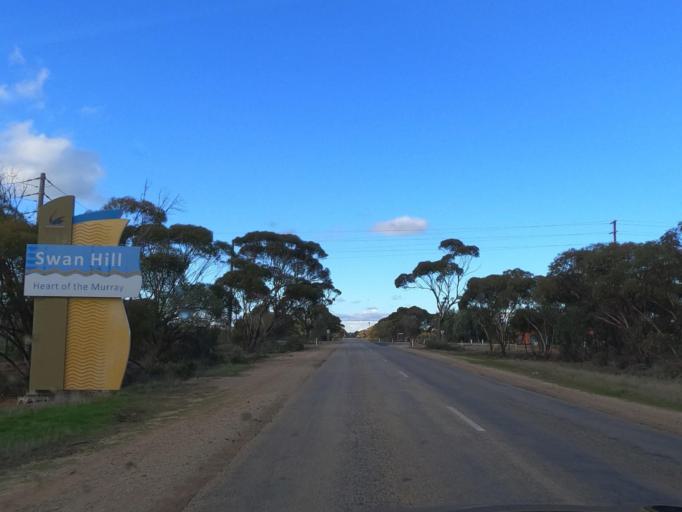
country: AU
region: Victoria
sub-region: Swan Hill
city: Swan Hill
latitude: -35.3460
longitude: 143.5225
